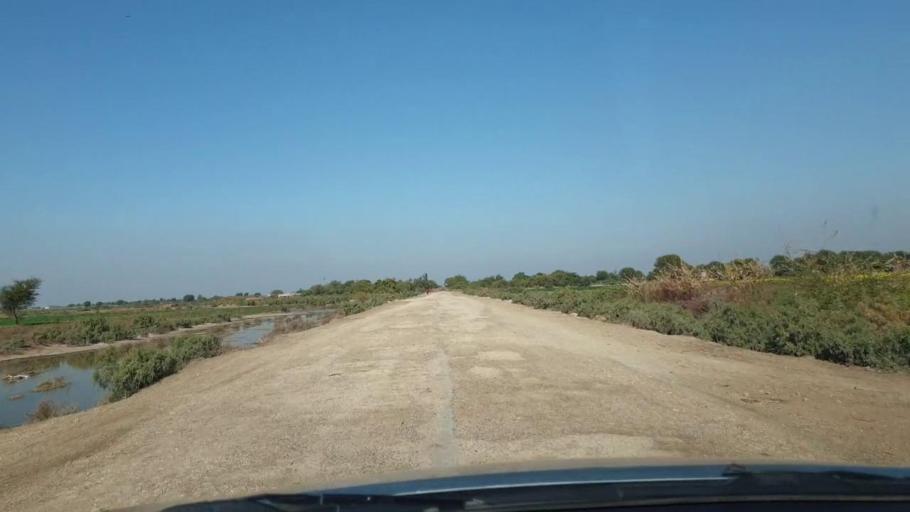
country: PK
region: Sindh
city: Jhol
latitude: 25.9257
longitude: 68.9080
